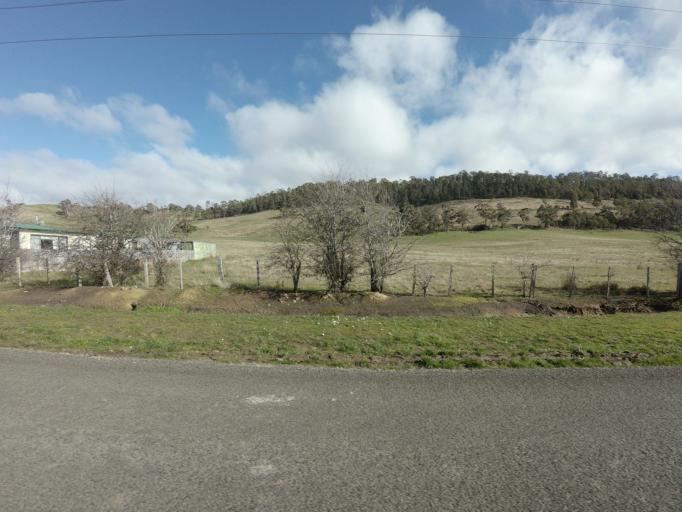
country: AU
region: Tasmania
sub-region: Derwent Valley
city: New Norfolk
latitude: -42.6119
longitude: 146.7119
